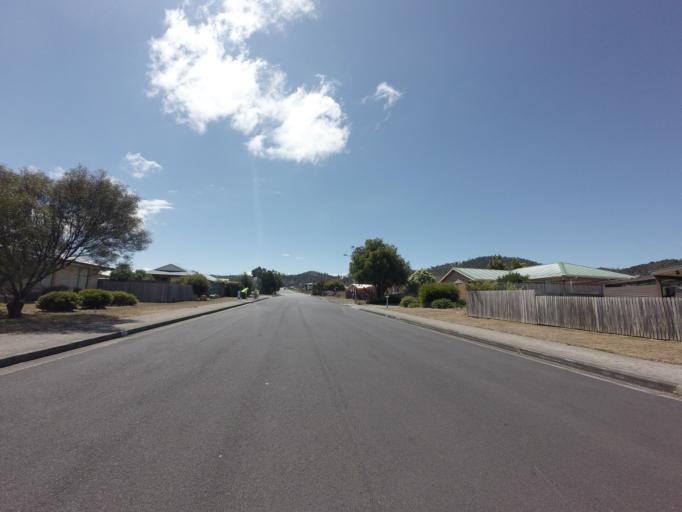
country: AU
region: Tasmania
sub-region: Clarence
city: Rokeby
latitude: -42.9018
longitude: 147.4512
